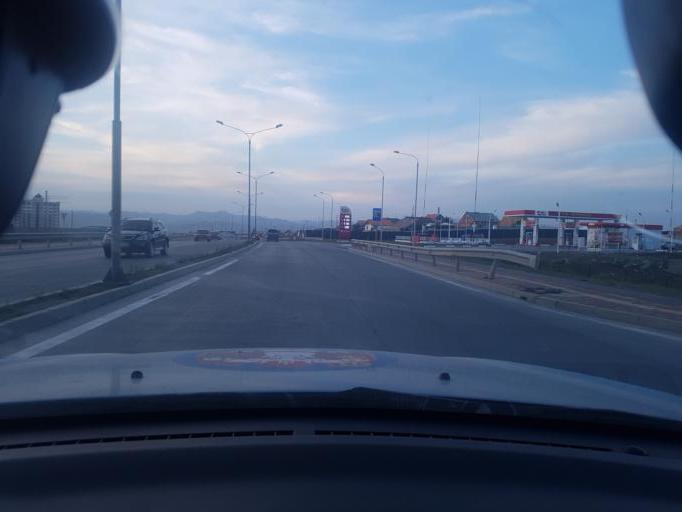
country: MN
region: Ulaanbaatar
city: Ulaanbaatar
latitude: 47.8624
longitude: 106.7882
